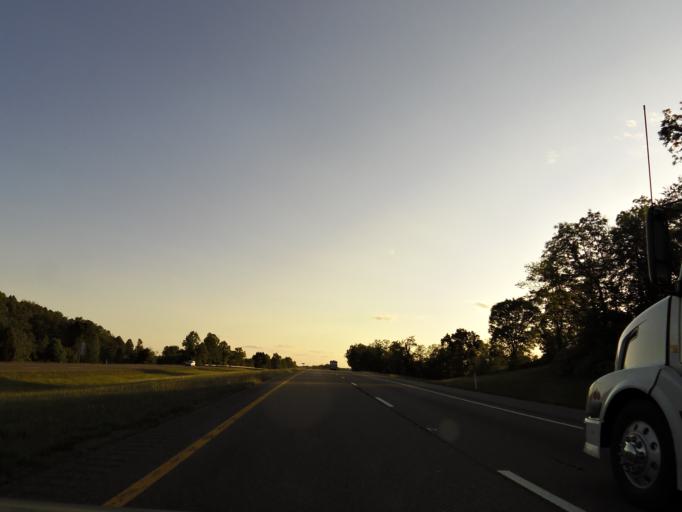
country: US
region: Tennessee
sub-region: Washington County
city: Spurgeon
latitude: 36.5127
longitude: -82.4155
